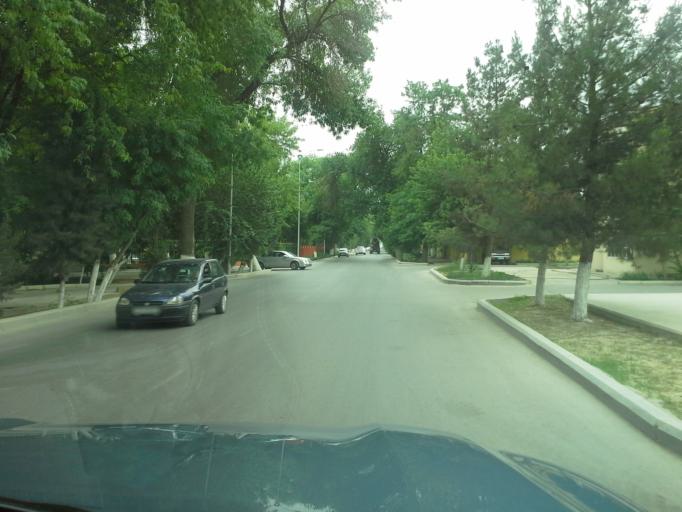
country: TM
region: Ahal
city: Ashgabat
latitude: 37.9537
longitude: 58.3647
